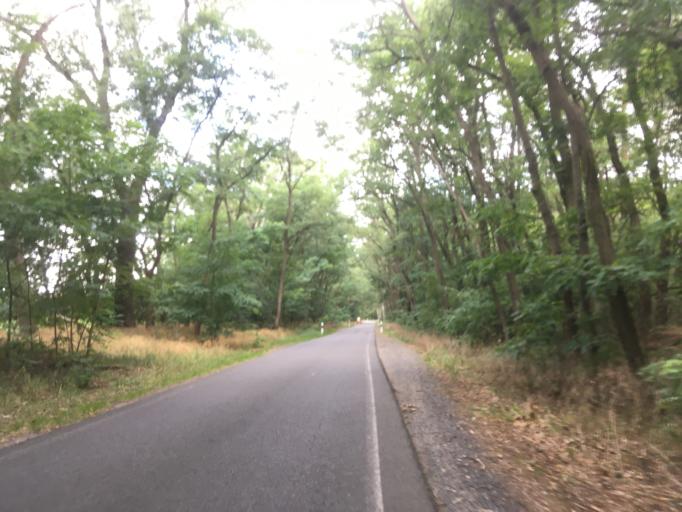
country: DE
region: Brandenburg
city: Bestensee
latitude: 52.2499
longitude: 13.7679
